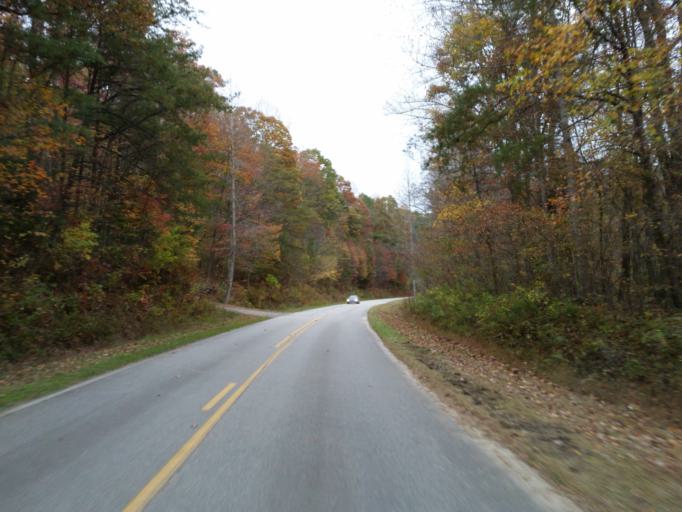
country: US
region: Georgia
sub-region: Fannin County
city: Blue Ridge
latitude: 34.6862
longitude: -84.2667
